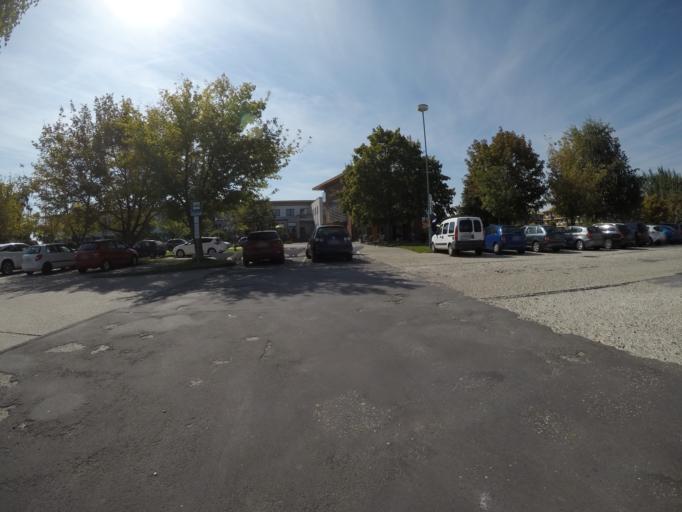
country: SK
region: Trnavsky
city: Dunajska Streda
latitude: 47.9854
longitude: 17.6094
